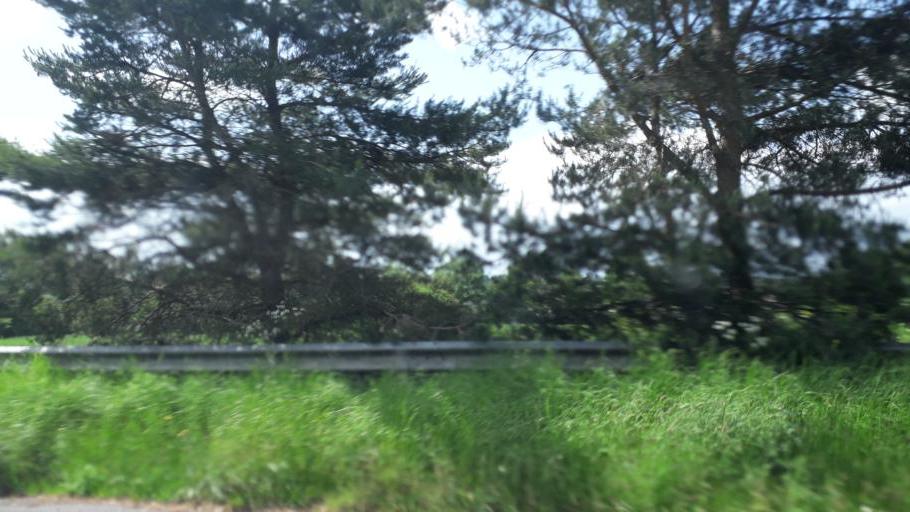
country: IE
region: Leinster
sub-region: Kildare
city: Moone
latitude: 53.0044
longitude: -6.8048
